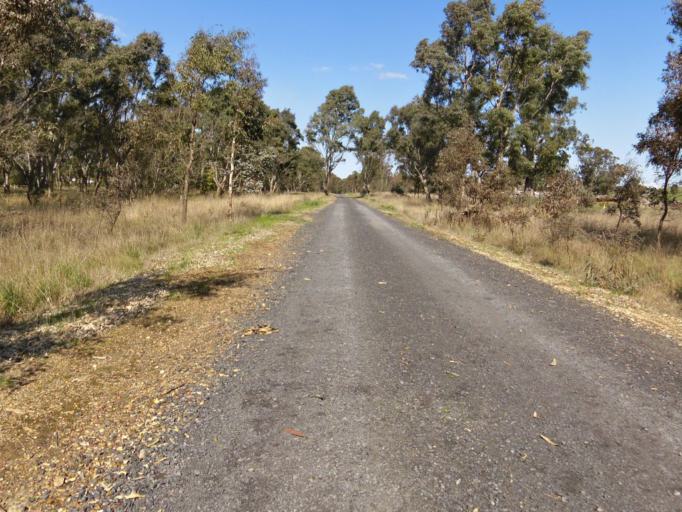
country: AU
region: Victoria
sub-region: Murrindindi
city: Alexandra
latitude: -36.9923
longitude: 145.7385
